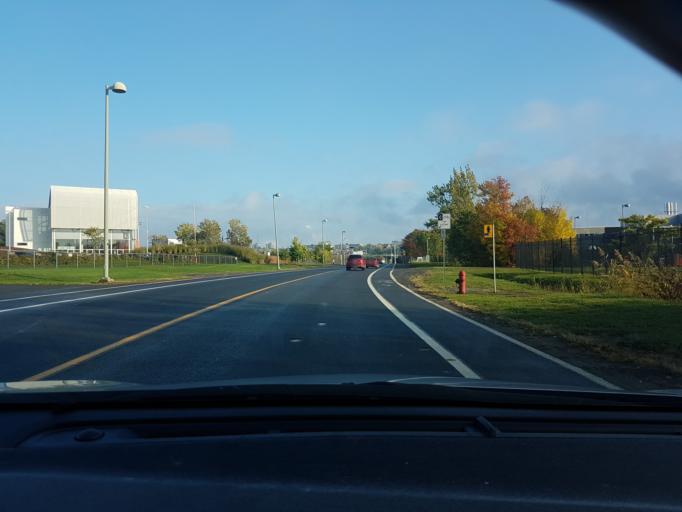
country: CA
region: Quebec
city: L'Ancienne-Lorette
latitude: 46.7973
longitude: -71.2957
